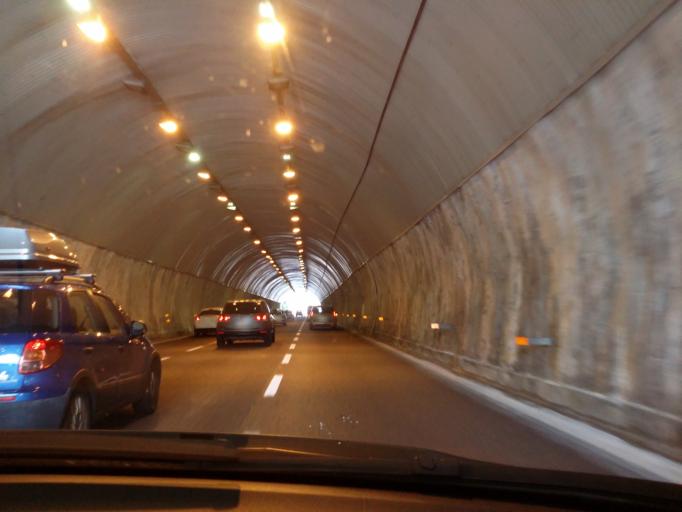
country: IT
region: Liguria
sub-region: Provincia di Genova
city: Cogoleto
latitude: 44.3985
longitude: 8.6631
